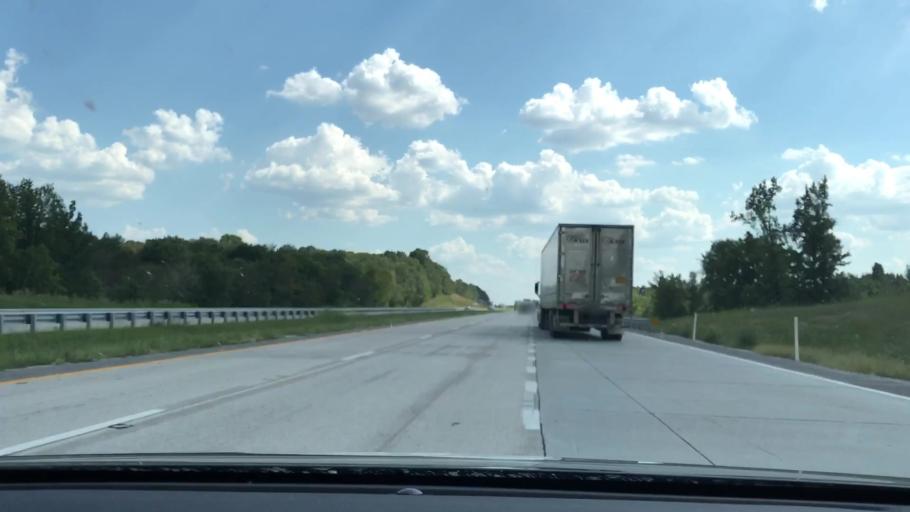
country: US
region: Kentucky
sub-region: Ohio County
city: Oak Grove
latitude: 37.3800
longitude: -86.8066
